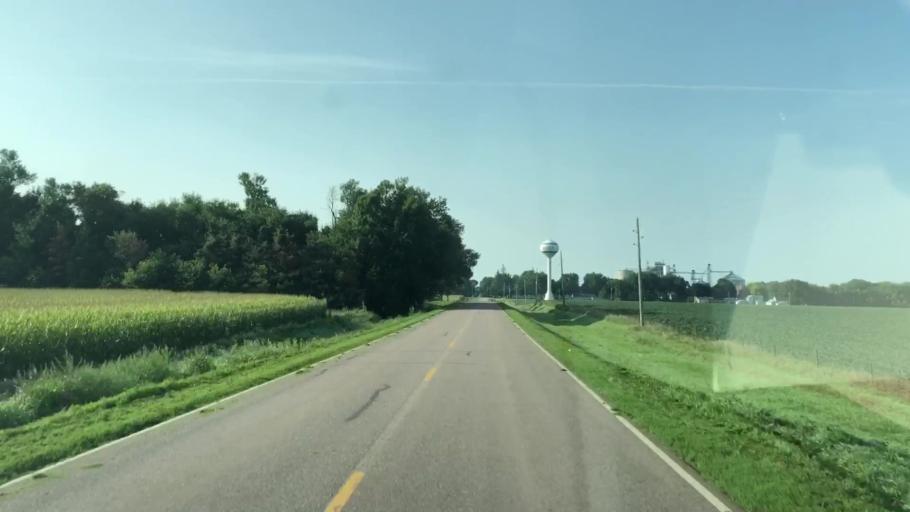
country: US
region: Iowa
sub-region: Sioux County
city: Hull
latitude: 43.1988
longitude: -96.0004
